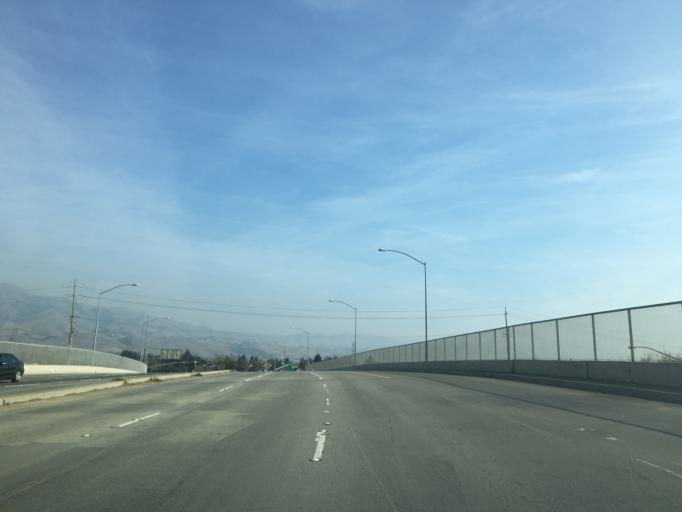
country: US
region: California
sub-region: Santa Clara County
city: Milpitas
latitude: 37.4543
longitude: -121.9240
